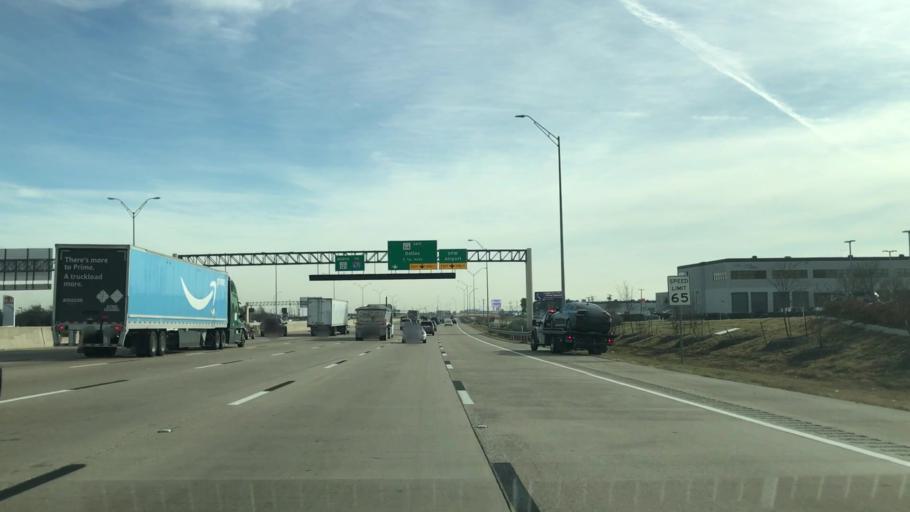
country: US
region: Texas
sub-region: Tarrant County
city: Grapevine
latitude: 32.9225
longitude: -97.0718
